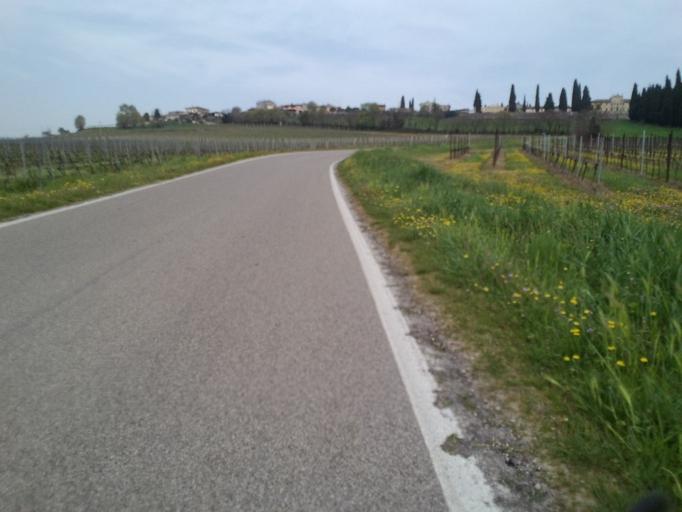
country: IT
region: Veneto
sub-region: Provincia di Verona
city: Rosegaferro
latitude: 45.3700
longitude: 10.7989
